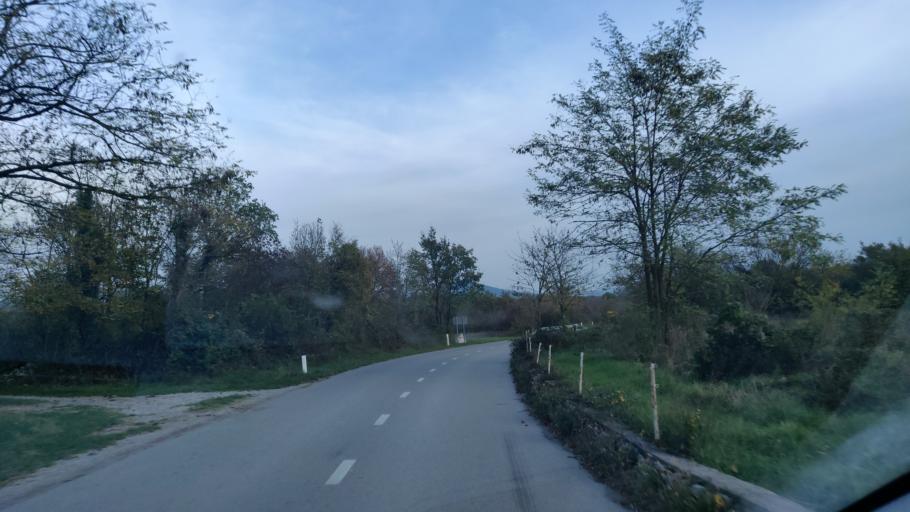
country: SI
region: Sezana
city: Sezana
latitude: 45.7594
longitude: 13.9138
